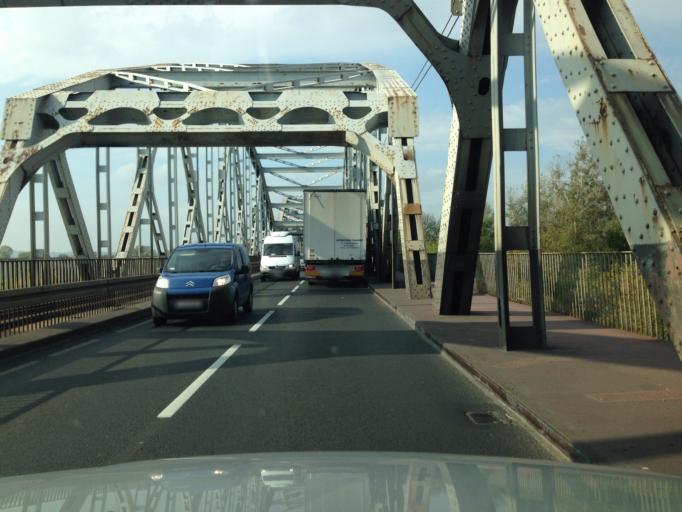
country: PL
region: Kujawsko-Pomorskie
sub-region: Grudziadz
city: Grudziadz
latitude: 53.4854
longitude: 18.7350
